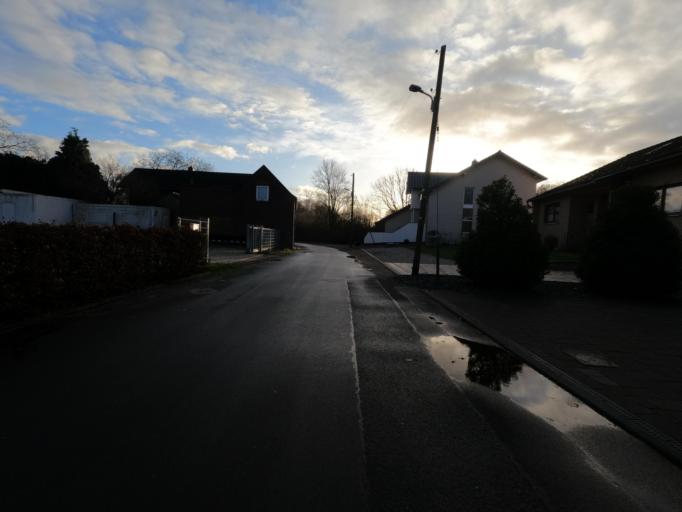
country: DE
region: North Rhine-Westphalia
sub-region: Regierungsbezirk Koln
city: Heinsberg
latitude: 51.0910
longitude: 6.0707
